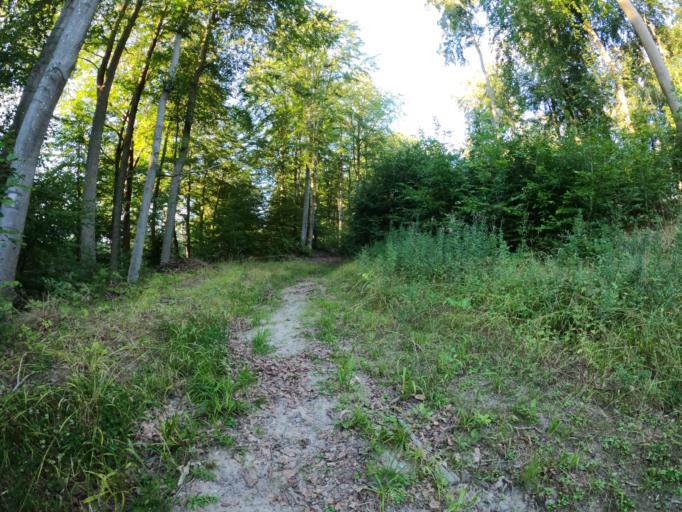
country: PL
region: West Pomeranian Voivodeship
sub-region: Powiat drawski
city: Zlocieniec
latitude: 53.6497
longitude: 15.9131
